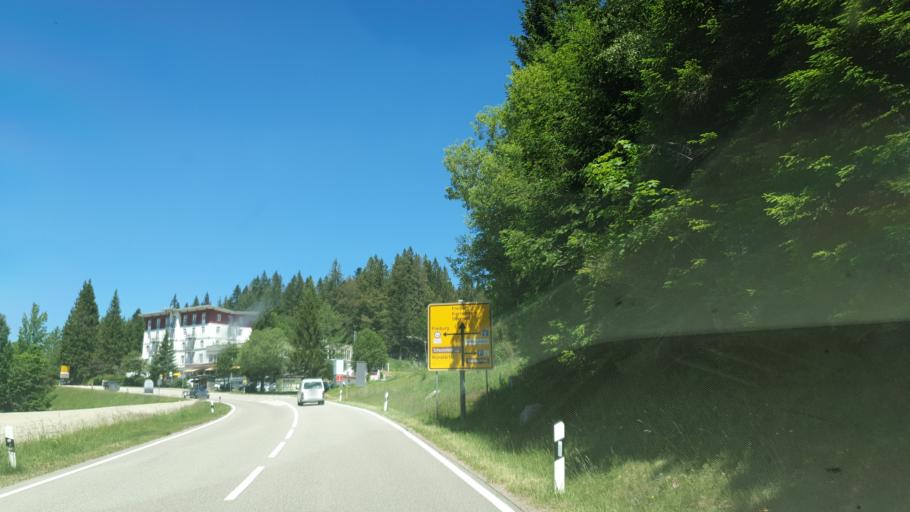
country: DE
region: Baden-Wuerttemberg
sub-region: Freiburg Region
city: Wieden
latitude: 47.8746
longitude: 7.9119
